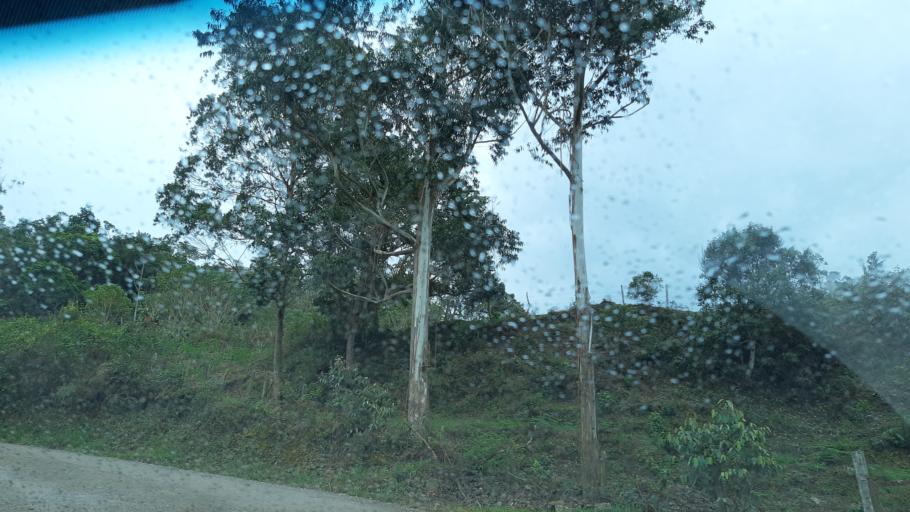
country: CO
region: Boyaca
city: Chivor
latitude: 4.9624
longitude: -73.3166
